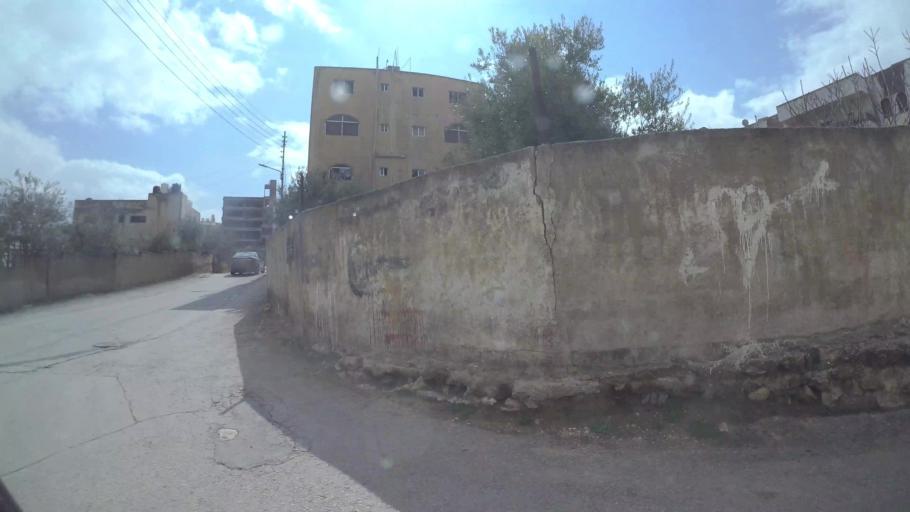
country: JO
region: Amman
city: Al Jubayhah
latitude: 32.0353
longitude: 35.8246
